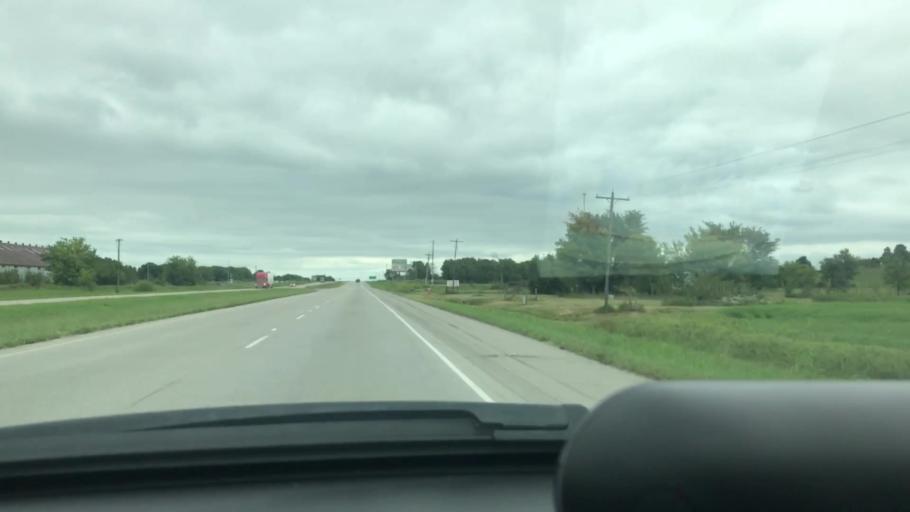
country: US
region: Oklahoma
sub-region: Mayes County
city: Chouteau
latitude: 36.1023
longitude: -95.3619
